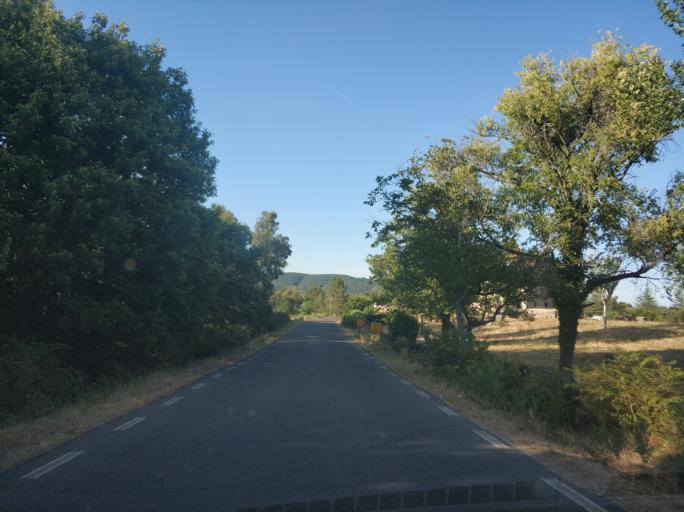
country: ES
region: Castille and Leon
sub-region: Provincia de Salamanca
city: Miranda del Castanar
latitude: 40.4848
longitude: -5.9851
